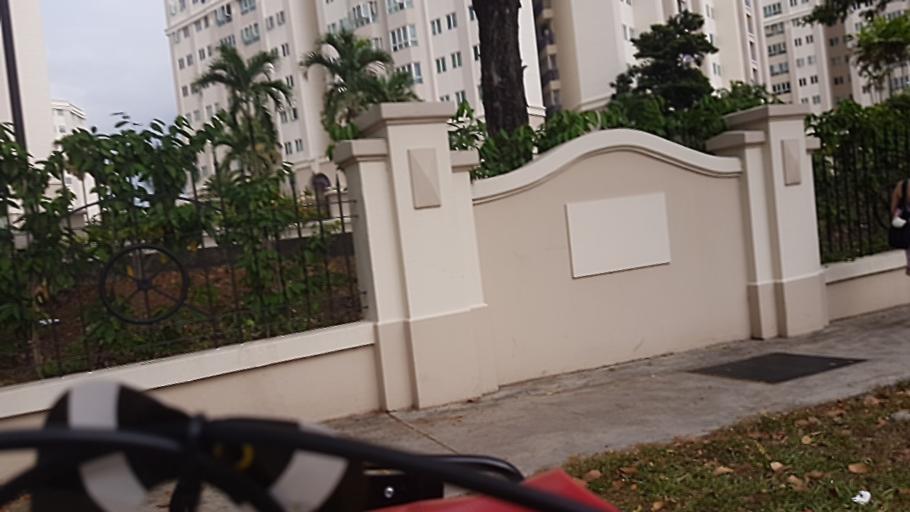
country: SG
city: Singapore
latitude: 1.3488
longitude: 103.9573
